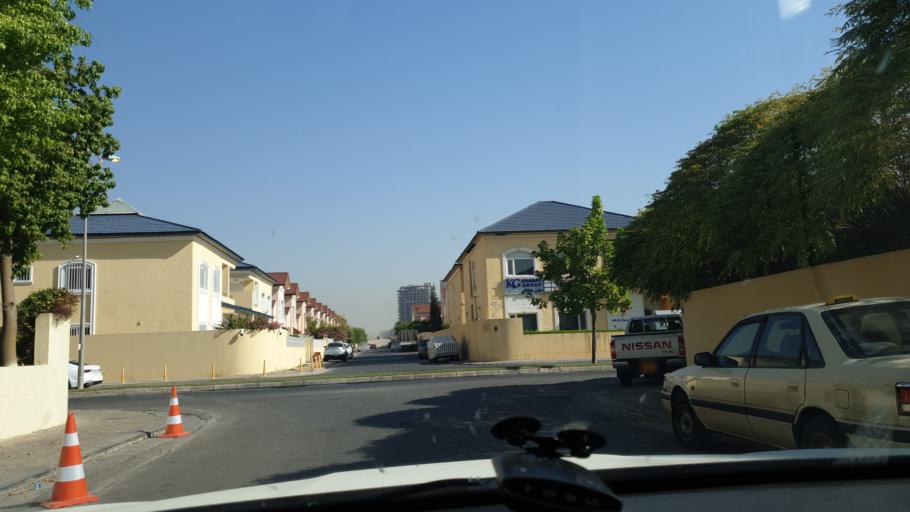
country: IQ
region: Arbil
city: Erbil
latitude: 36.1868
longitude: 43.9651
